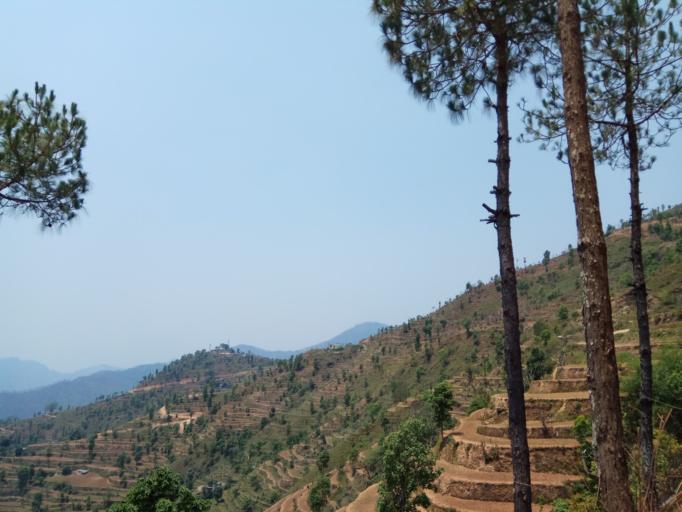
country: NP
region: Central Region
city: Kirtipur
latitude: 27.8957
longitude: 85.0753
